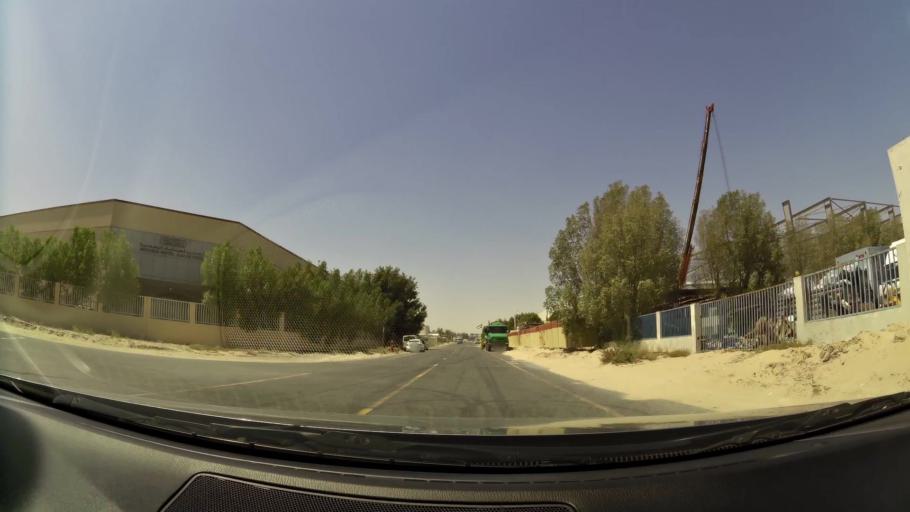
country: AE
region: Dubai
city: Dubai
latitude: 24.9789
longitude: 55.1870
